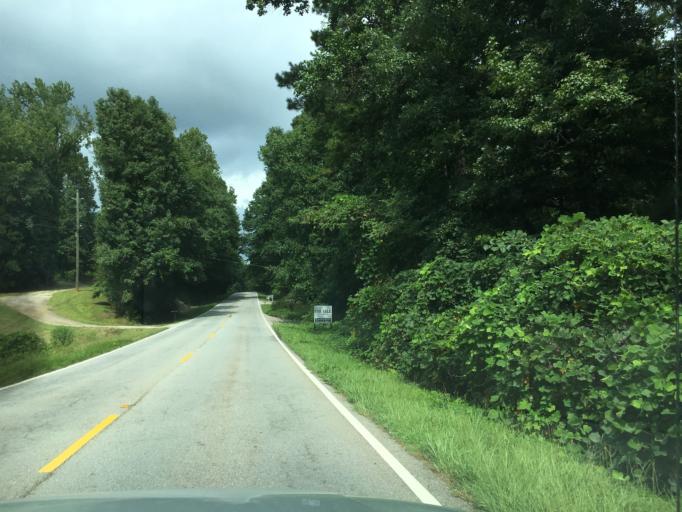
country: US
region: Georgia
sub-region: DeKalb County
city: Pine Mountain
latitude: 33.6282
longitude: -84.0775
